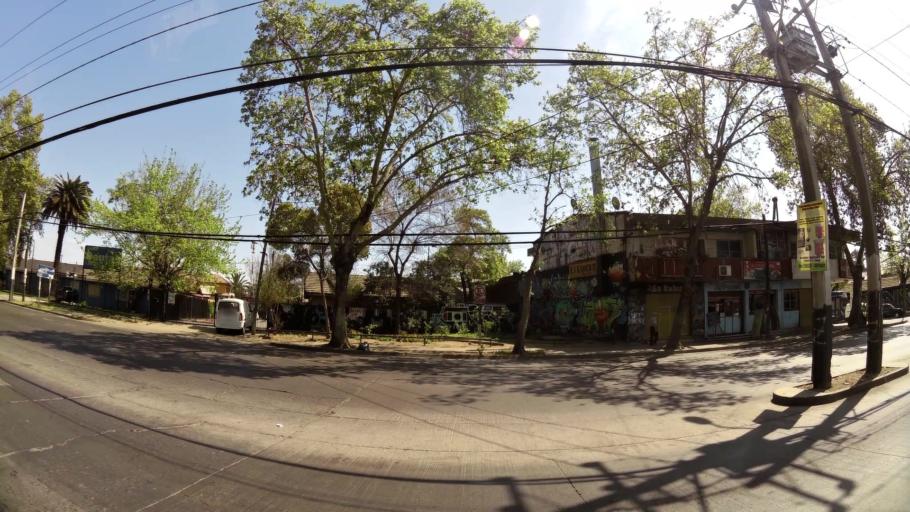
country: CL
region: Santiago Metropolitan
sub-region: Provincia de Maipo
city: San Bernardo
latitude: -33.5515
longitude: -70.6729
